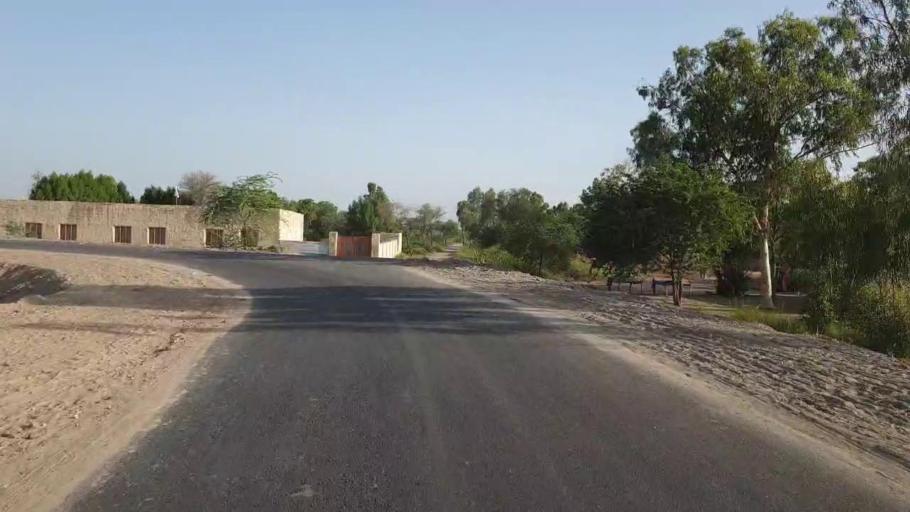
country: PK
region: Sindh
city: Jam Sahib
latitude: 26.3480
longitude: 68.5562
